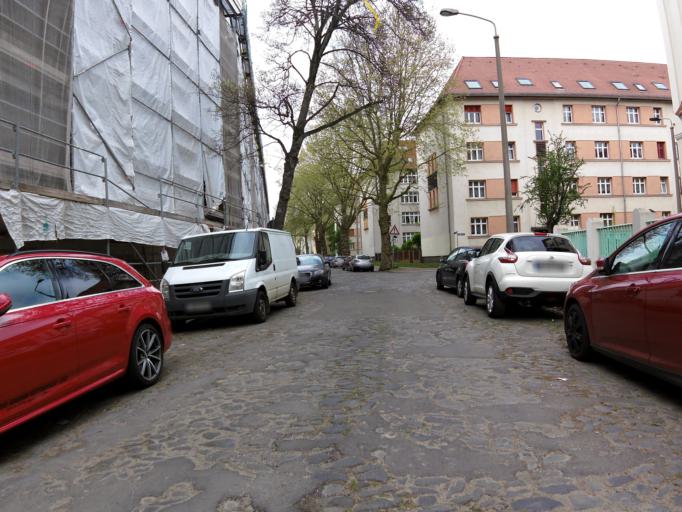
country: DE
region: Saxony
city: Leipzig
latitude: 51.3628
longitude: 12.3777
